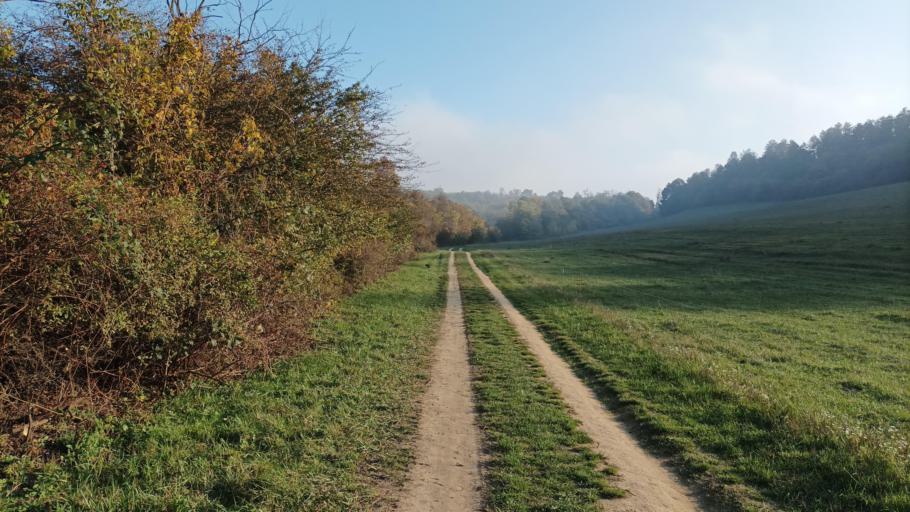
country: HU
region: Tolna
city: Szentgalpuszta
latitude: 46.3258
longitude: 18.6086
